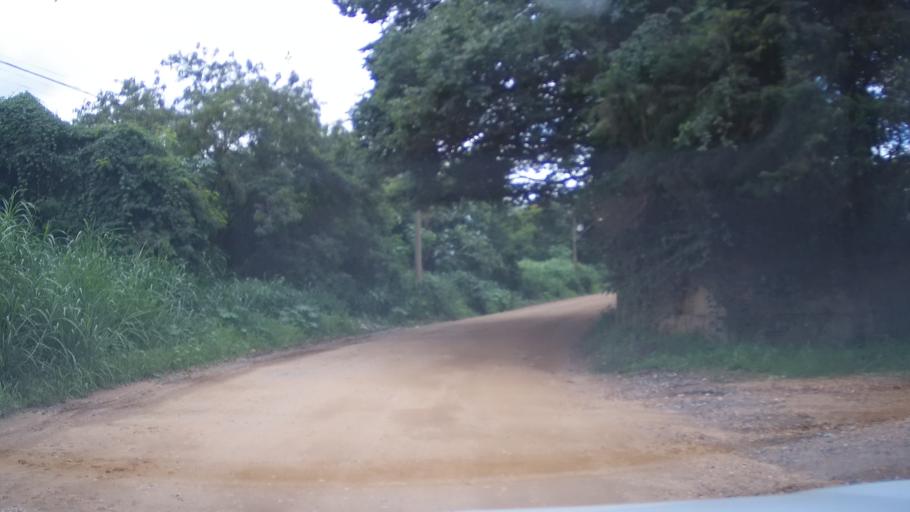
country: BR
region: Sao Paulo
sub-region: Valinhos
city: Valinhos
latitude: -22.9932
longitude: -46.9888
